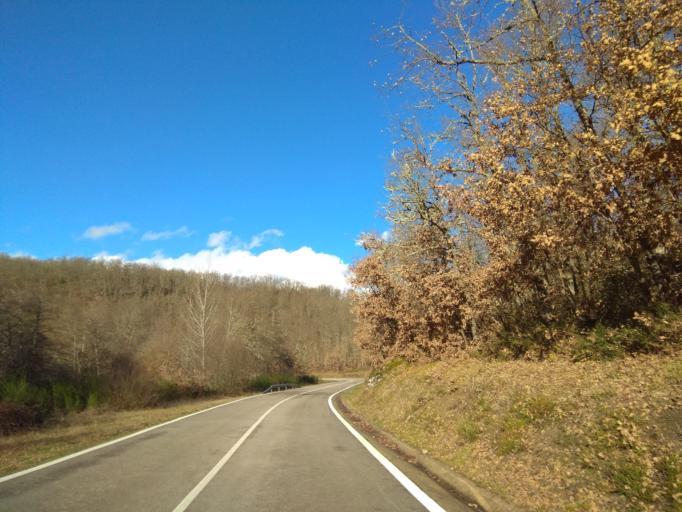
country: ES
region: Cantabria
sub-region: Provincia de Cantabria
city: San Martin de Elines
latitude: 42.9029
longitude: -3.8781
